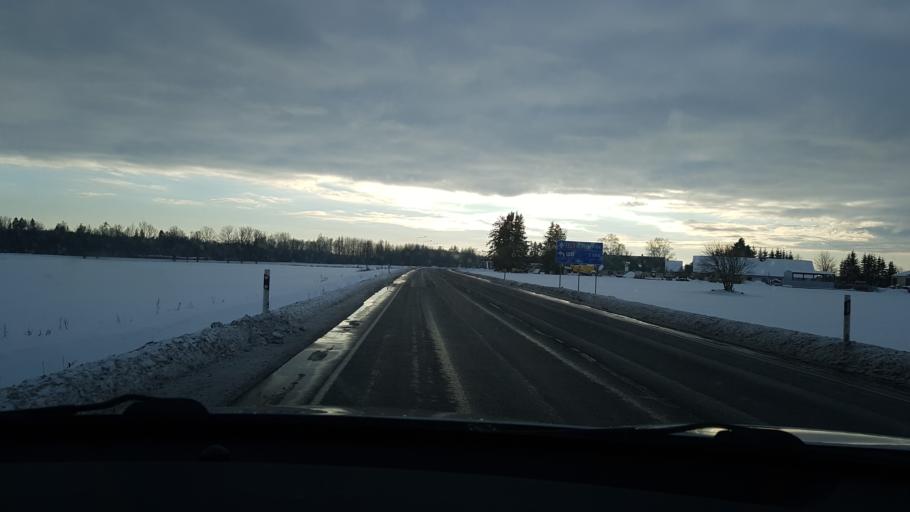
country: EE
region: Jaervamaa
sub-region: Paide linn
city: Paide
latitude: 58.9427
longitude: 25.6426
